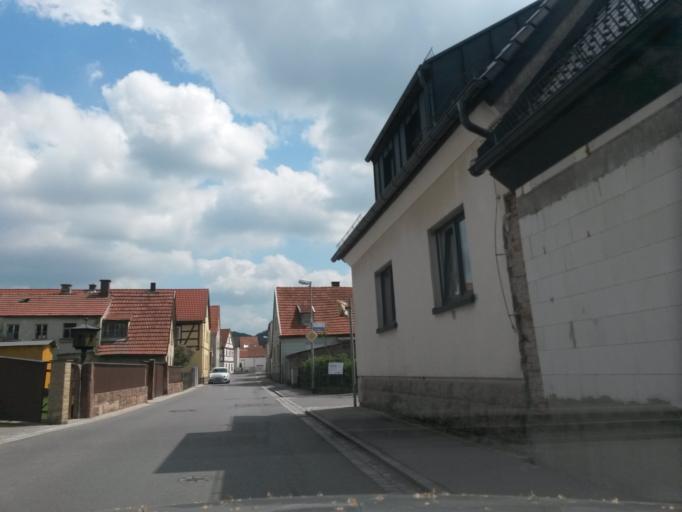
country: DE
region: Bavaria
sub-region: Regierungsbezirk Unterfranken
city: Nudlingen
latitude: 50.2228
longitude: 10.1226
